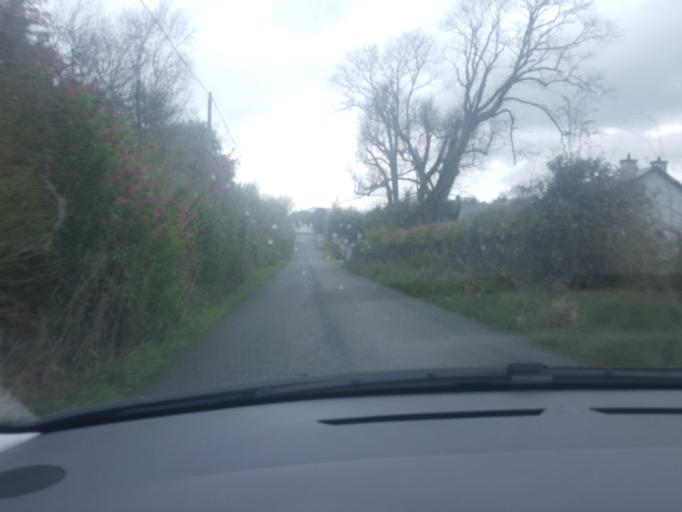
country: IE
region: Munster
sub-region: Ciarrai
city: Cill Airne
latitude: 52.0726
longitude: -9.5074
